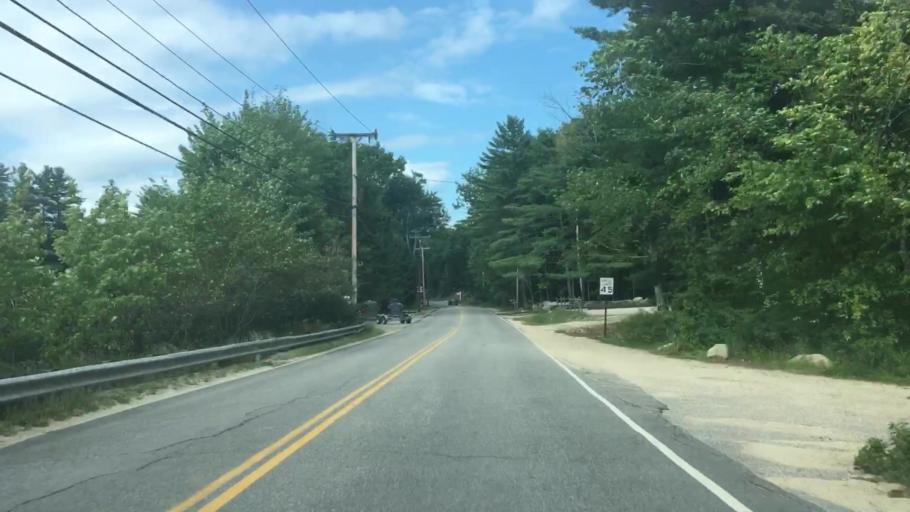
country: US
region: Maine
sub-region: Oxford County
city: Oxford
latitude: 44.1103
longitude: -70.5073
